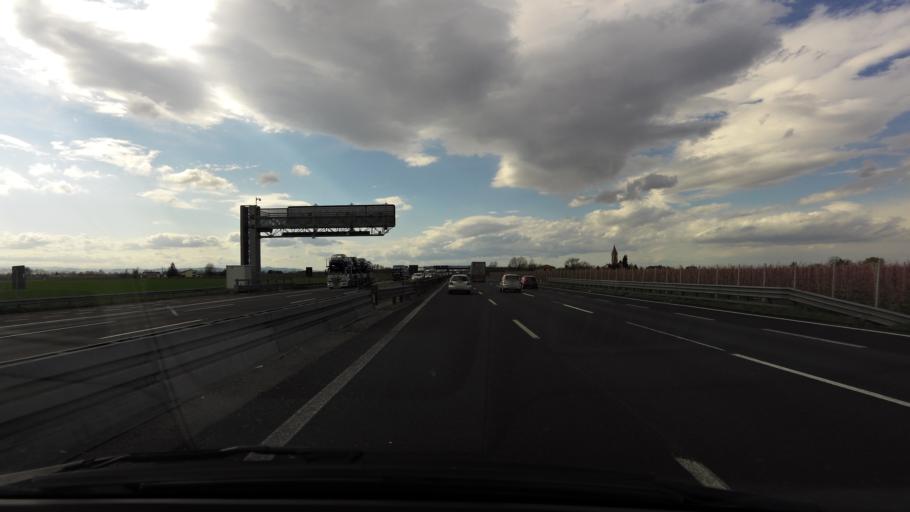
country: IT
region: Emilia-Romagna
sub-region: Provincia di Ravenna
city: Castel Bolognese
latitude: 44.3572
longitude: 11.8054
